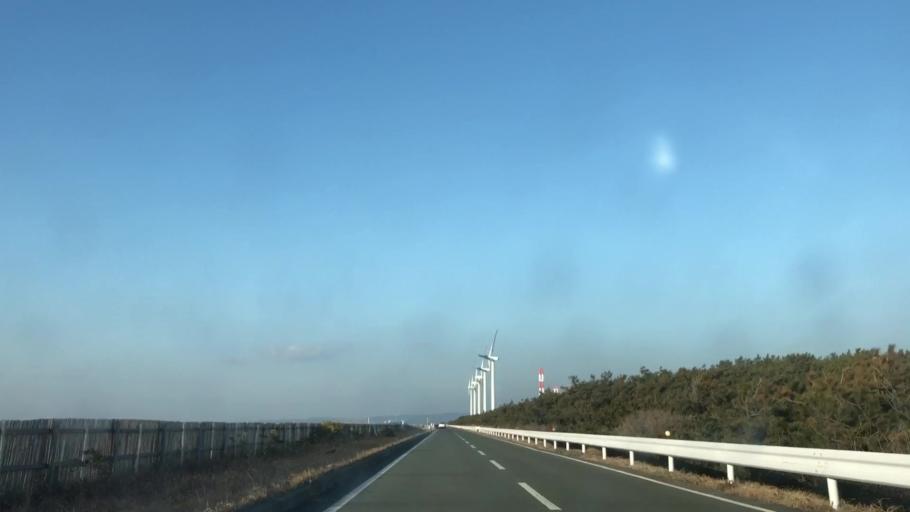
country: JP
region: Aichi
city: Toyohama
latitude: 34.6299
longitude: 137.0478
